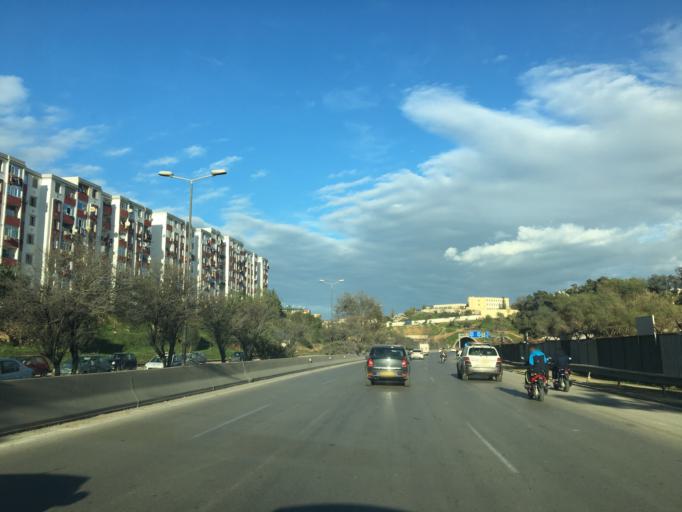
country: DZ
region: Tipaza
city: Baraki
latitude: 36.7219
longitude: 3.1064
